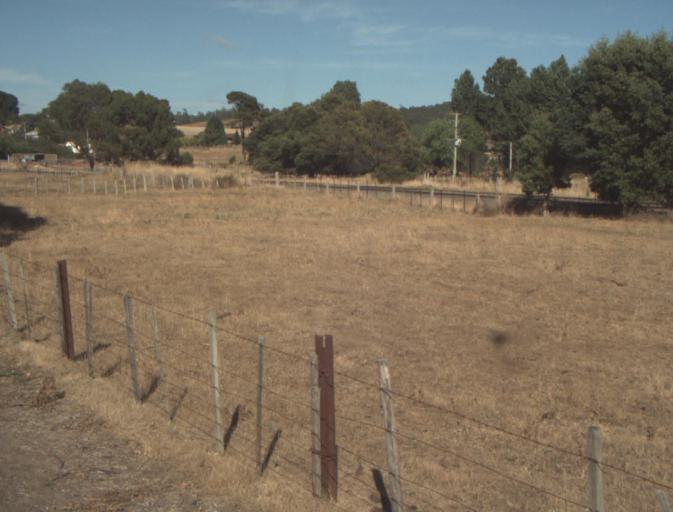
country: AU
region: Tasmania
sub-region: Launceston
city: Mayfield
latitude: -41.1789
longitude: 147.2274
